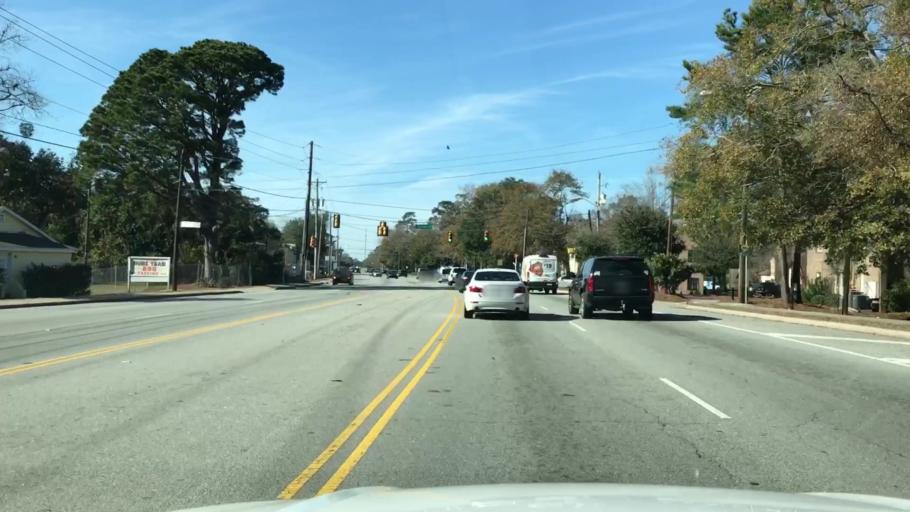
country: US
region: South Carolina
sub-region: Charleston County
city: North Charleston
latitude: 32.7970
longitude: -79.9967
